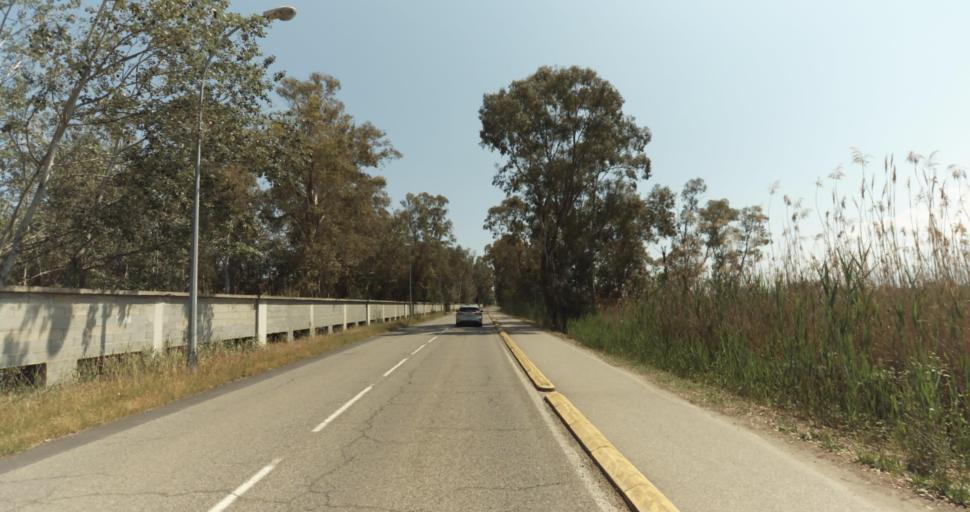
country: FR
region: Corsica
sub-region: Departement de la Haute-Corse
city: Biguglia
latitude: 42.6140
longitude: 9.4797
